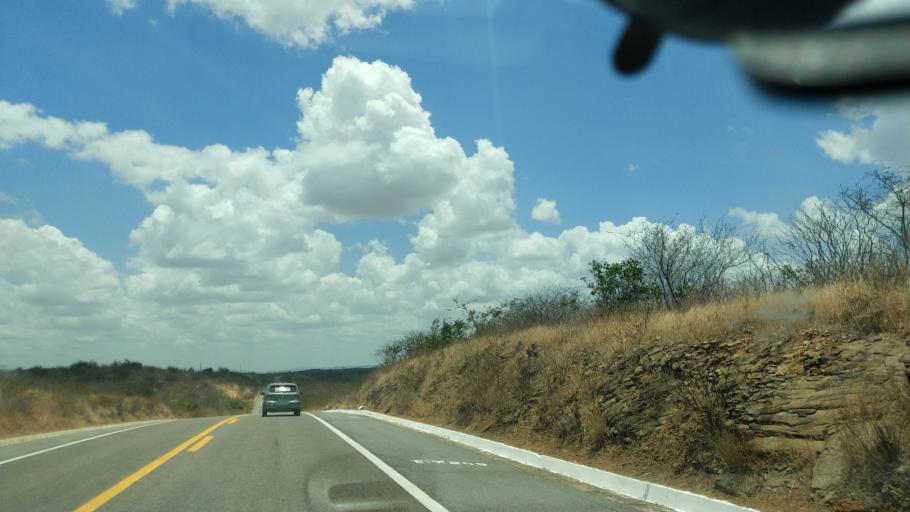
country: BR
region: Rio Grande do Norte
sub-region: Cerro Cora
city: Cerro Cora
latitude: -6.1971
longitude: -36.2667
